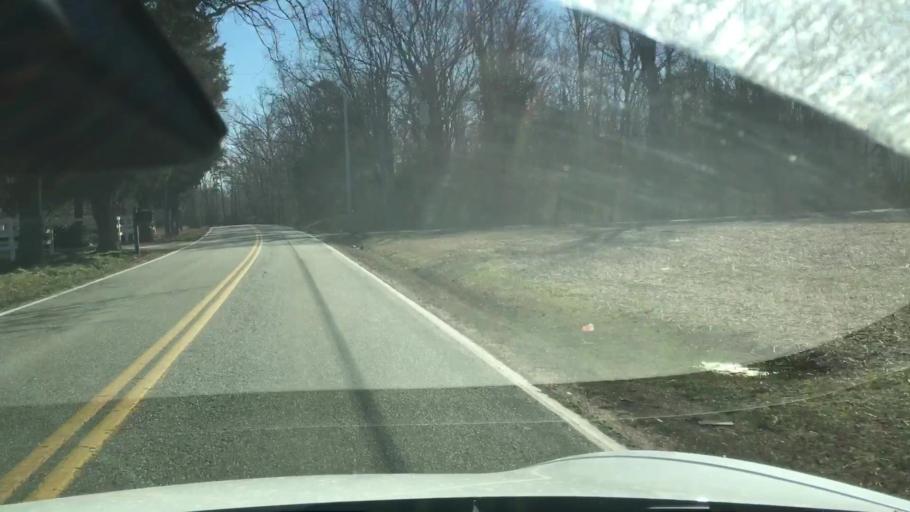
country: US
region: Virginia
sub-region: Henrico County
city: Short Pump
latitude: 37.5895
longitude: -77.7563
